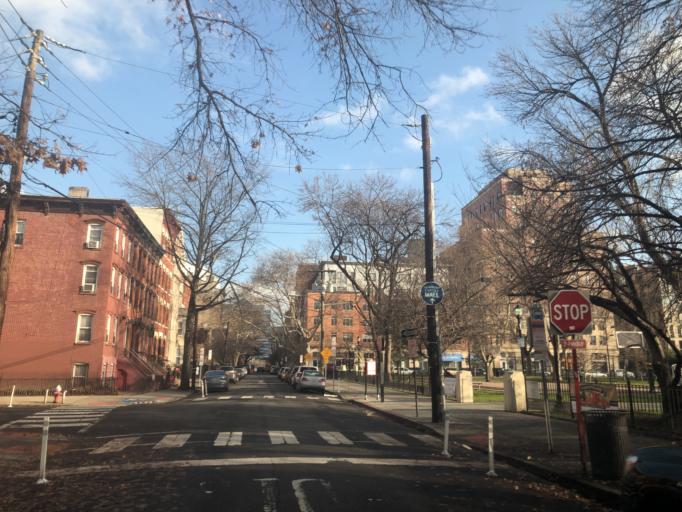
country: US
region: New Jersey
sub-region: Hudson County
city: Hoboken
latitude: 40.7284
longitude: -74.0453
